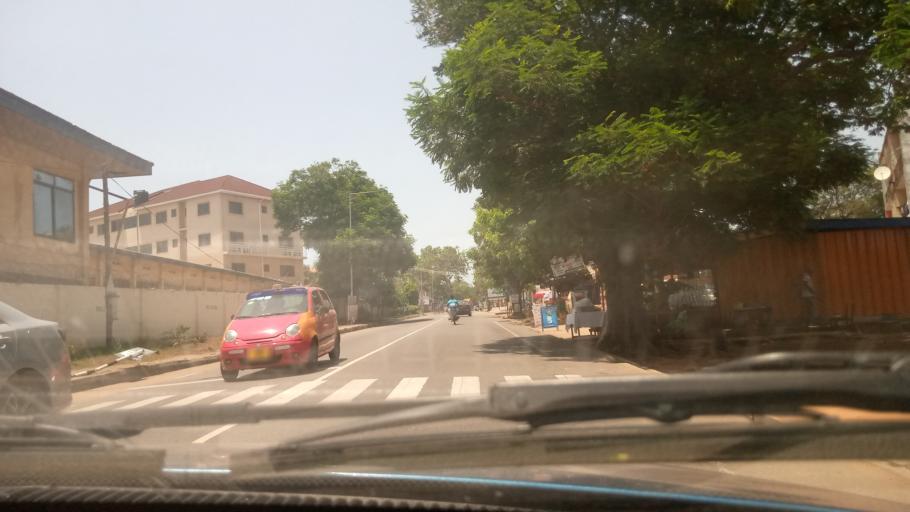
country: GH
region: Greater Accra
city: Accra
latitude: 5.5482
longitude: -0.2314
